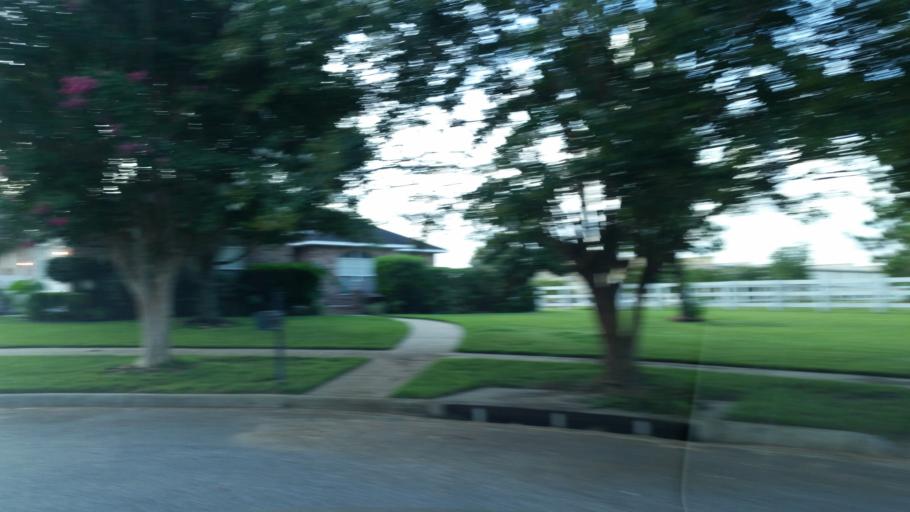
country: US
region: Florida
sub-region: Escambia County
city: Ensley
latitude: 30.5369
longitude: -87.3101
